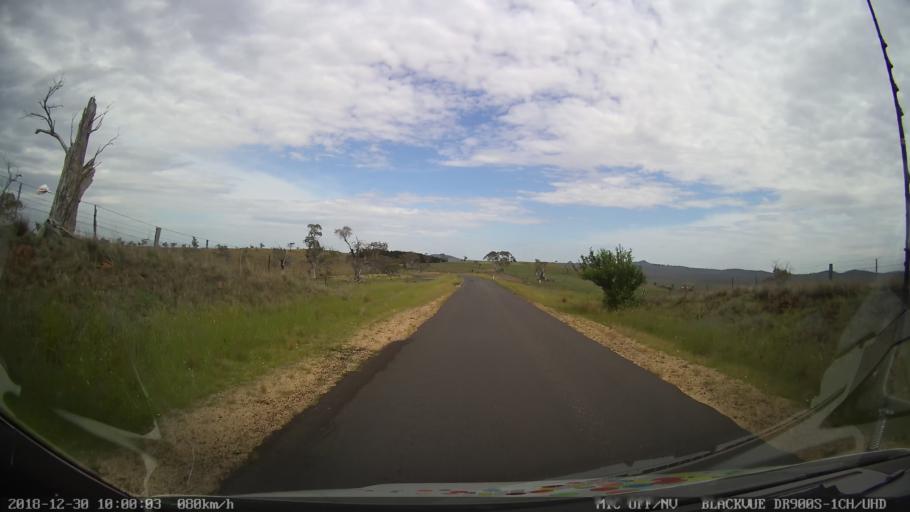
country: AU
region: New South Wales
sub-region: Cooma-Monaro
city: Cooma
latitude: -36.5191
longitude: 149.2026
